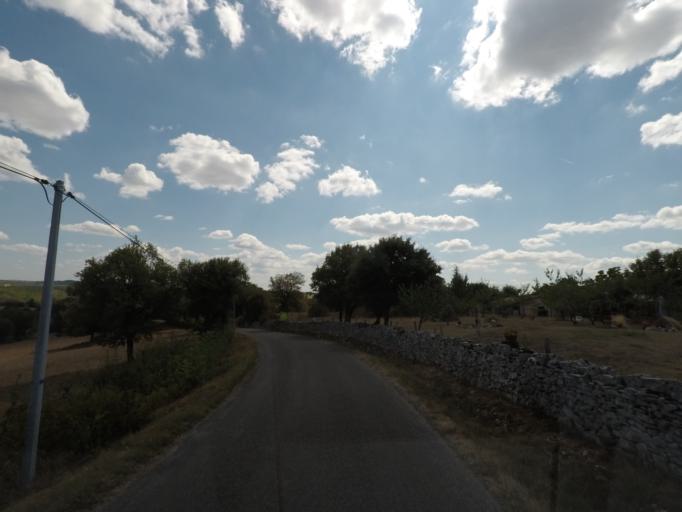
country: FR
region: Midi-Pyrenees
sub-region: Departement du Lot
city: Cajarc
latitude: 44.5265
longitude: 1.6598
